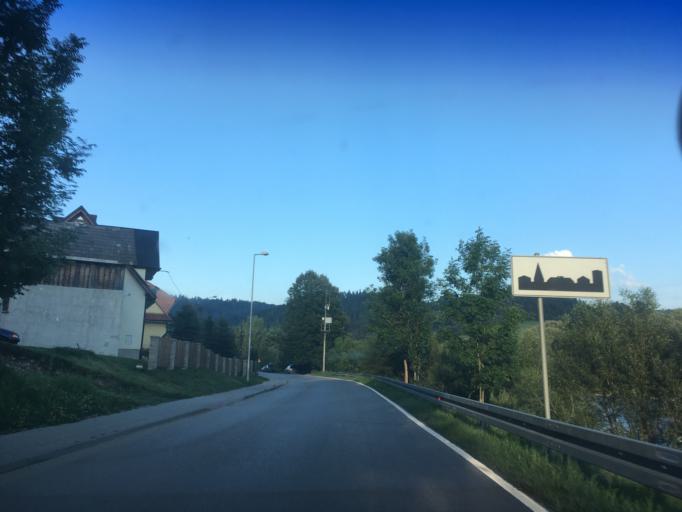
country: PL
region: Lesser Poland Voivodeship
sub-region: Powiat nowotarski
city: Kroscienko nad Dunajcem
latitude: 49.3925
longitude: 20.4007
